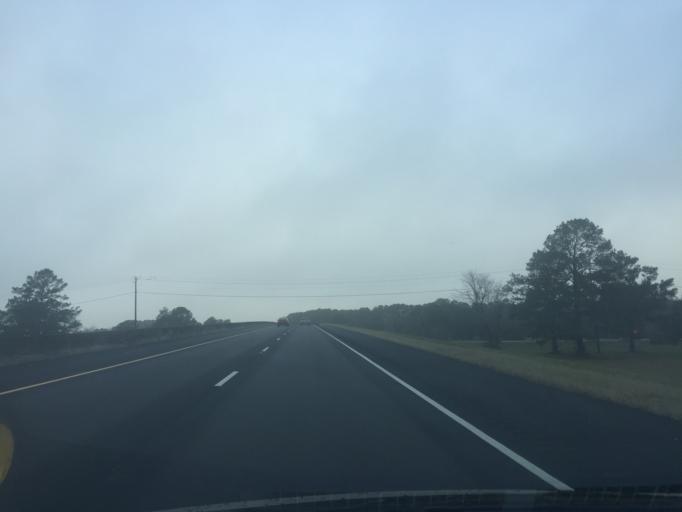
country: US
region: Georgia
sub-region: Chatham County
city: Georgetown
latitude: 31.9992
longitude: -81.2461
